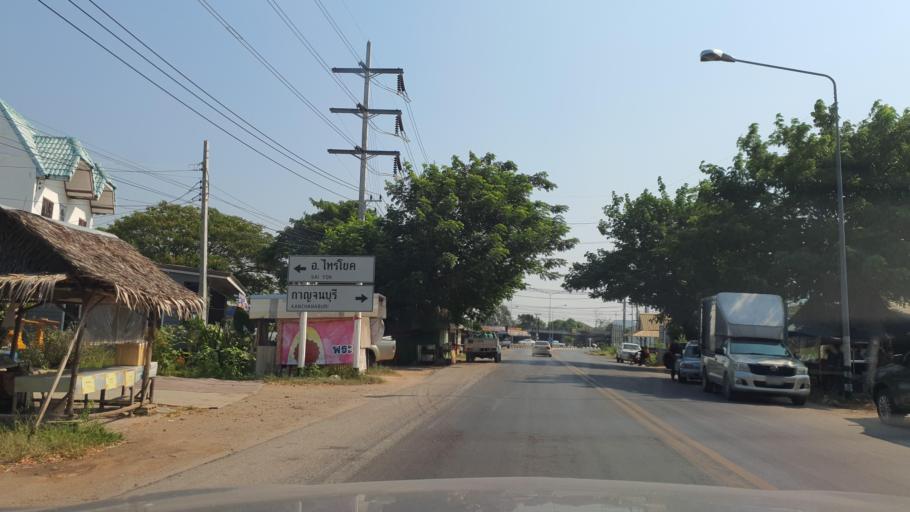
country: TH
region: Kanchanaburi
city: Kanchanaburi
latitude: 14.0587
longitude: 99.4771
